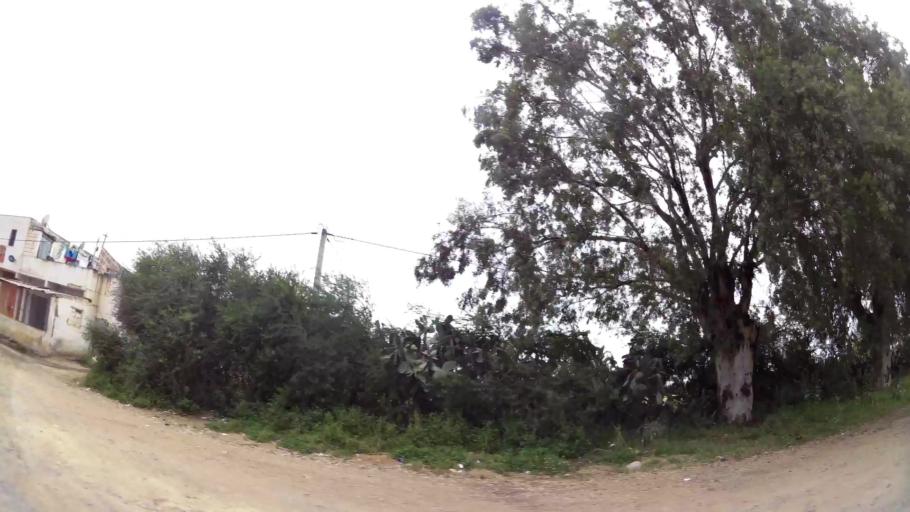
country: MA
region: Rabat-Sale-Zemmour-Zaer
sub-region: Khemisset
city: Tiflet
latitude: 33.8496
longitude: -6.2691
